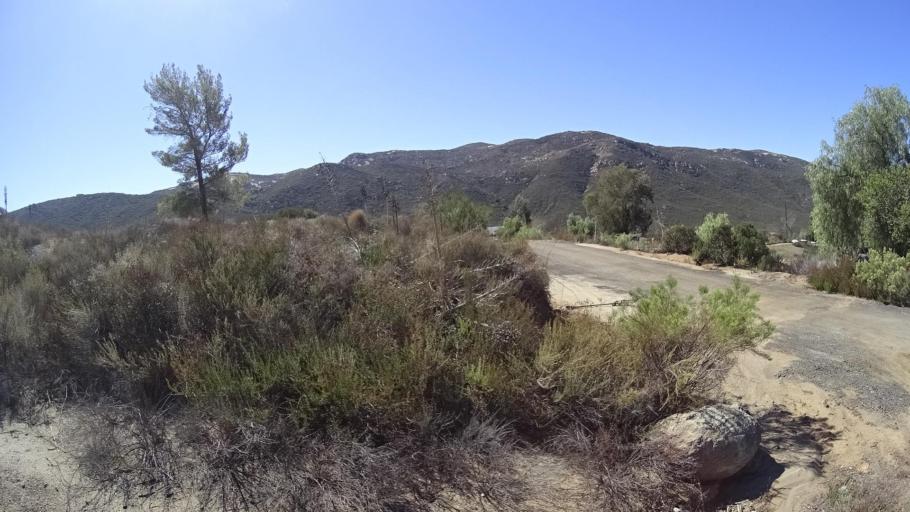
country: US
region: California
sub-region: San Diego County
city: Alpine
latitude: 32.7884
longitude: -116.7289
